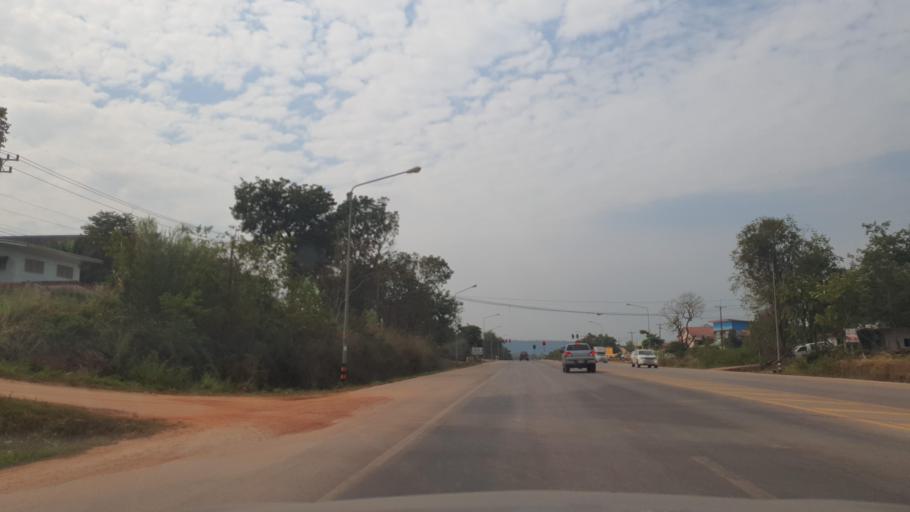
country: TH
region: Changwat Bueng Kan
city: Bung Khla
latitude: 18.2765
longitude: 103.8578
